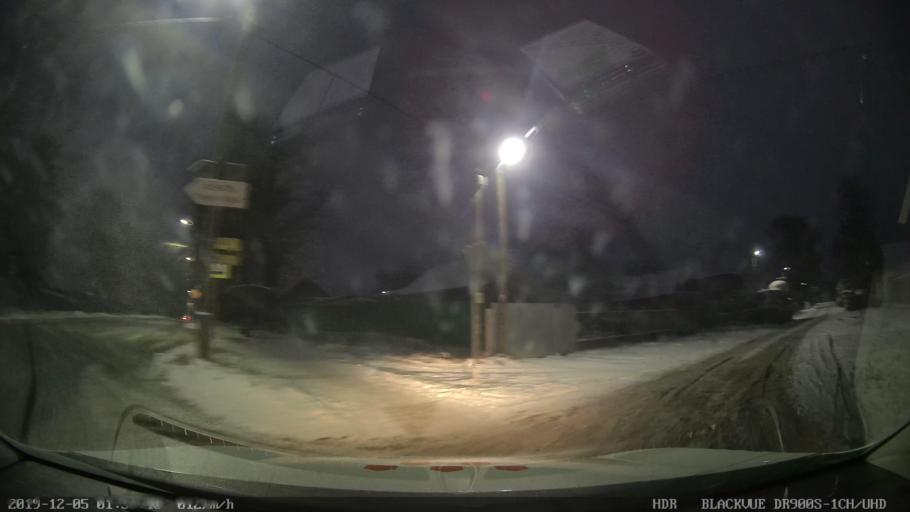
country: RU
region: Tatarstan
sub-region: Gorod Kazan'
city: Kazan
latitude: 55.7027
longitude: 49.1402
